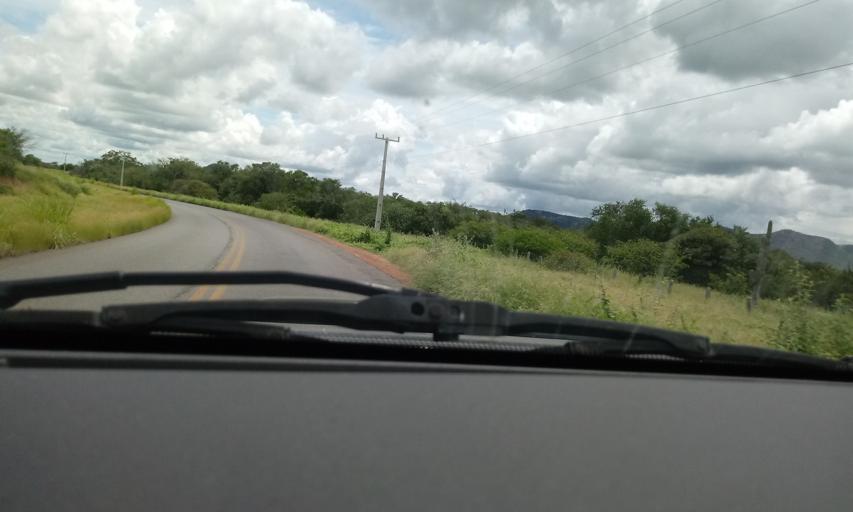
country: BR
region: Bahia
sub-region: Guanambi
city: Guanambi
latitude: -14.1686
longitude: -42.8071
